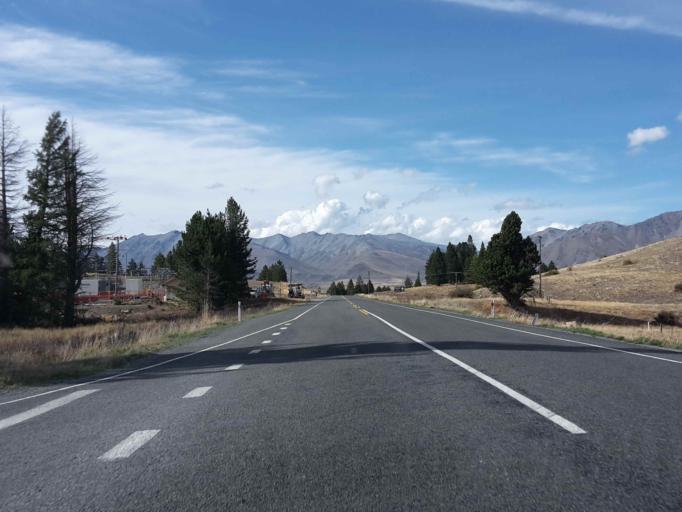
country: NZ
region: Canterbury
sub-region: Timaru District
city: Pleasant Point
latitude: -44.0023
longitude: 170.4547
